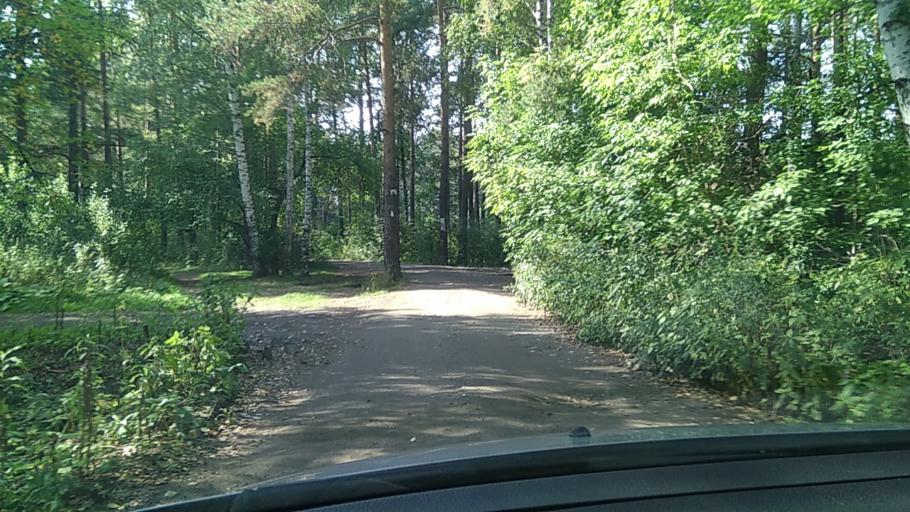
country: RU
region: Sverdlovsk
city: Yekaterinburg
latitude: 56.8901
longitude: 60.5598
